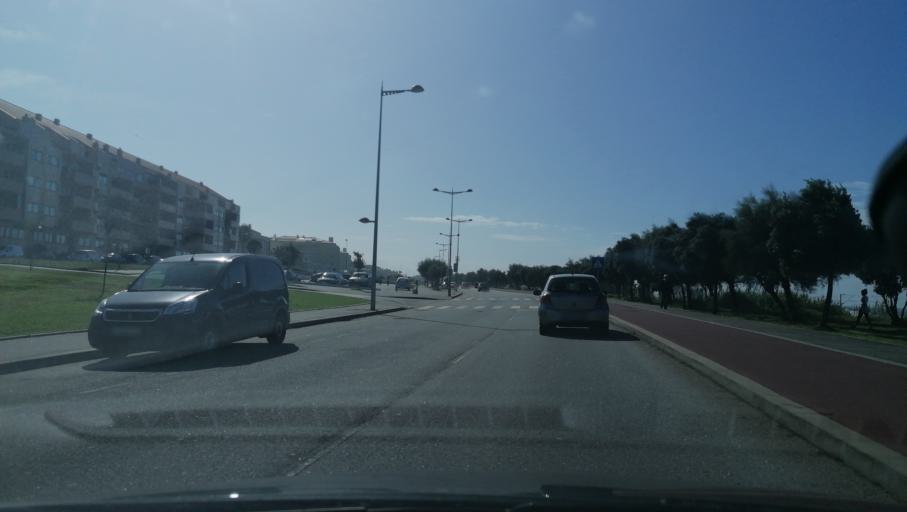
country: PT
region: Aveiro
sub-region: Espinho
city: Espinho
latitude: 41.0253
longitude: -8.6430
